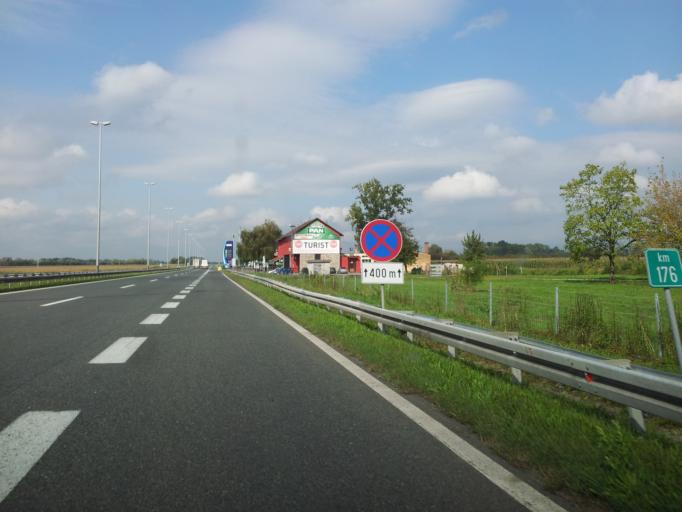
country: HR
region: Brodsko-Posavska
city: Vrbova
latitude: 45.2162
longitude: 17.5193
